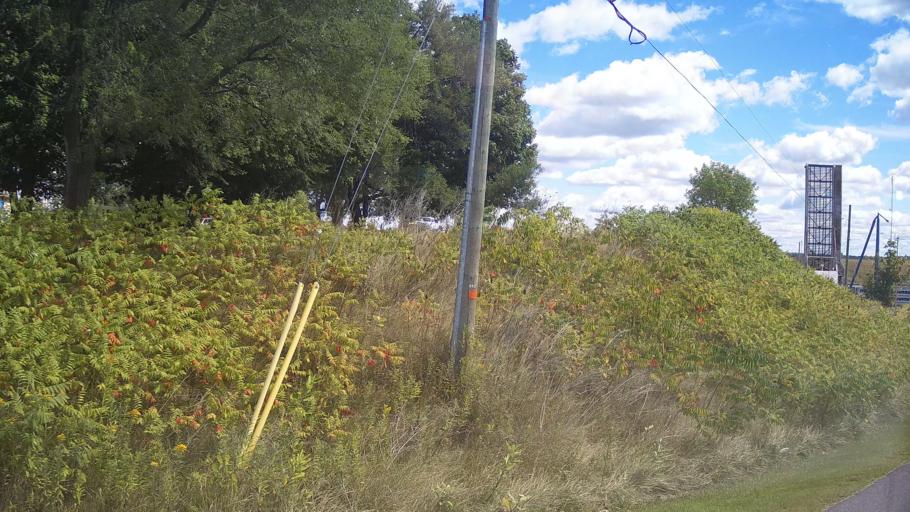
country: US
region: New York
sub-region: St. Lawrence County
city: Ogdensburg
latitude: 44.8337
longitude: -75.3129
